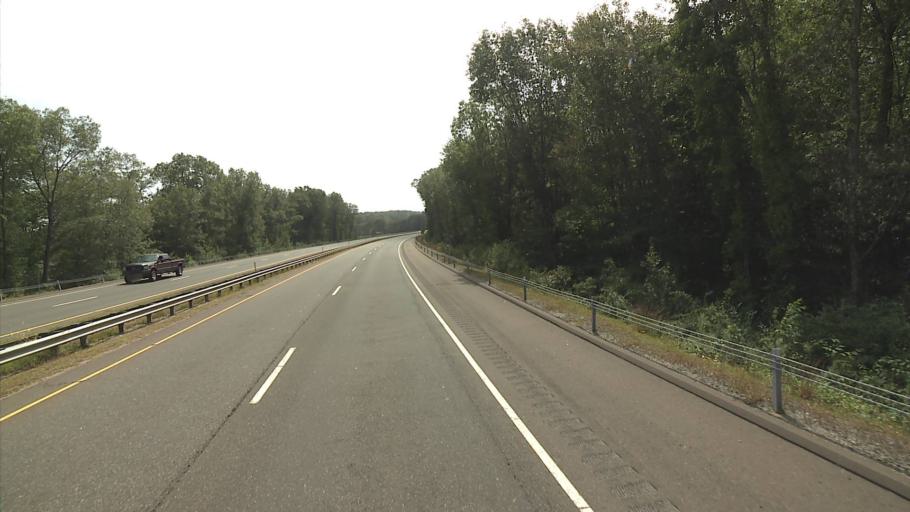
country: US
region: Connecticut
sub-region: New London County
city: Niantic
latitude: 41.3202
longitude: -72.2463
